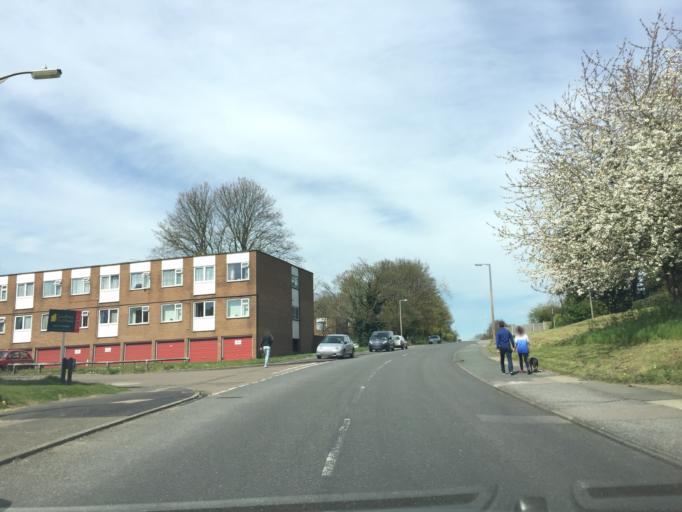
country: GB
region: England
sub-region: Essex
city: Harlow
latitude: 51.7630
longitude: 0.0848
